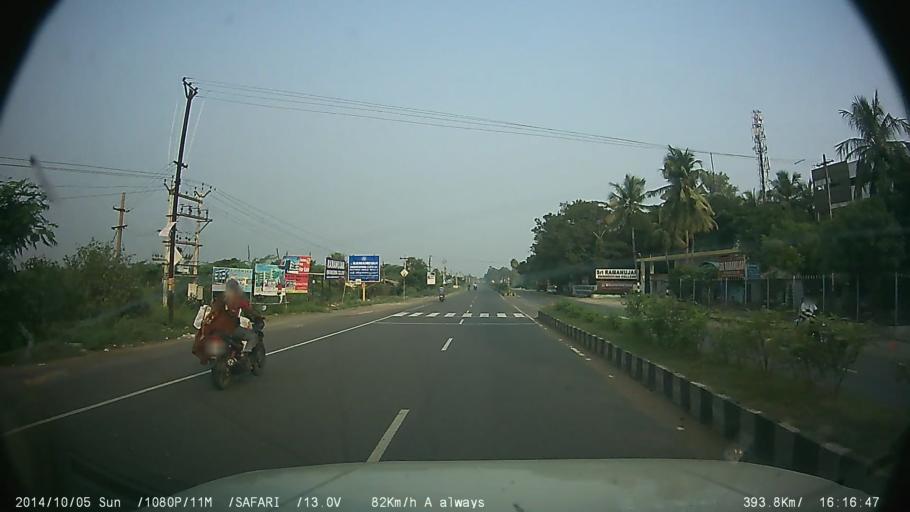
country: IN
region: Tamil Nadu
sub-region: Kancheepuram
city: Vandalur
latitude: 12.8676
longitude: 80.1146
